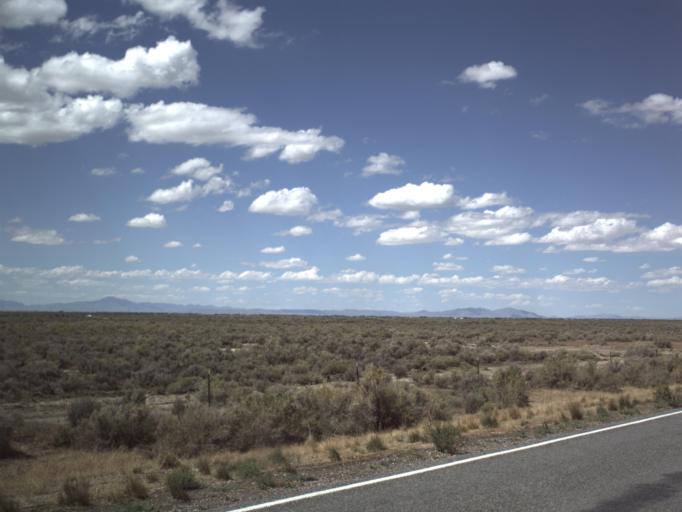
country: US
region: Utah
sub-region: Millard County
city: Delta
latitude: 39.2504
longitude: -112.4393
